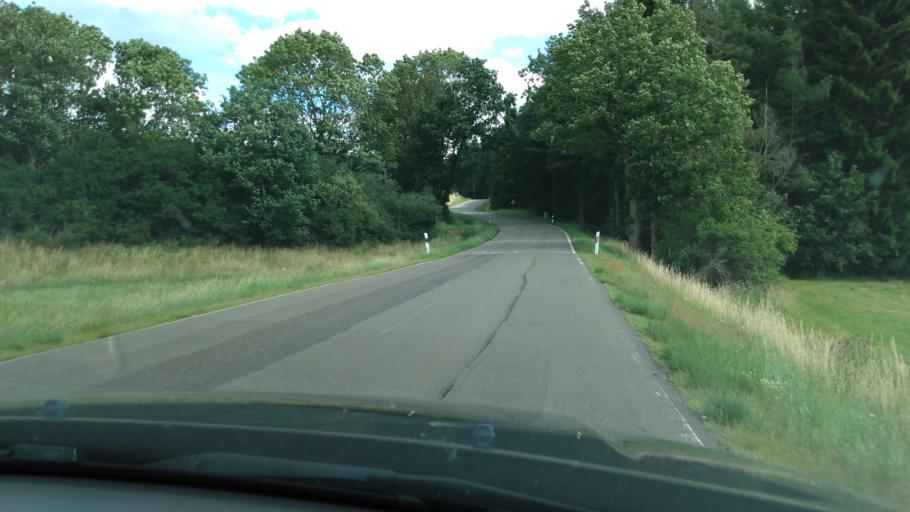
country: DE
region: Rheinland-Pfalz
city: Karl
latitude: 50.0570
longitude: 6.7914
